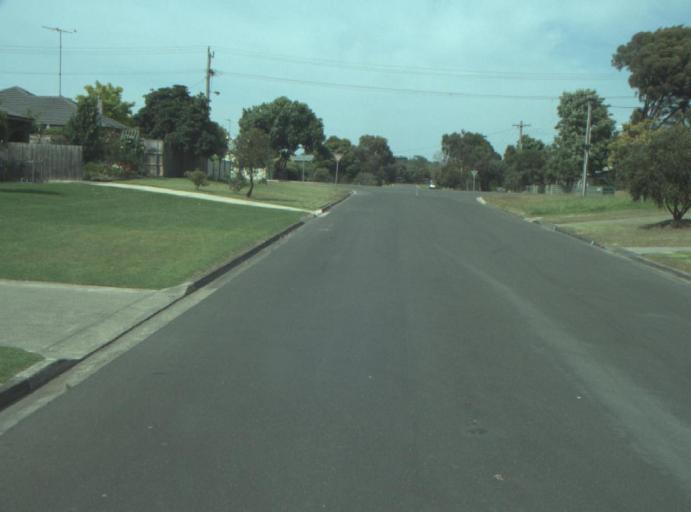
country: AU
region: Victoria
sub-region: Greater Geelong
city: Clifton Springs
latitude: -38.1745
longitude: 144.5668
